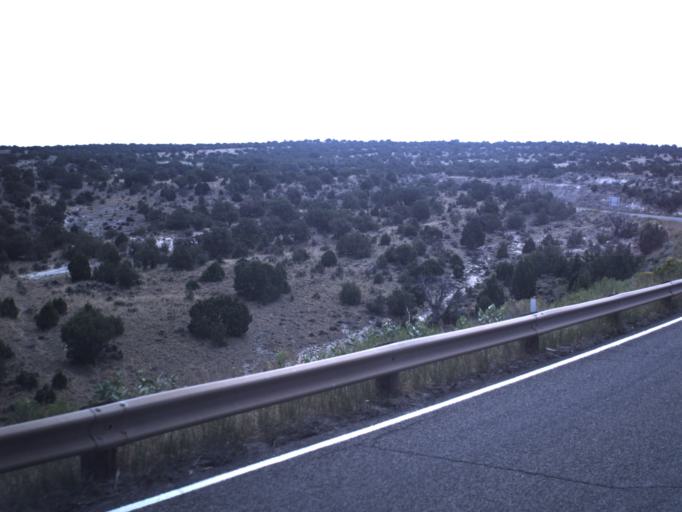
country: US
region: Utah
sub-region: Daggett County
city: Manila
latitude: 40.9401
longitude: -109.7134
